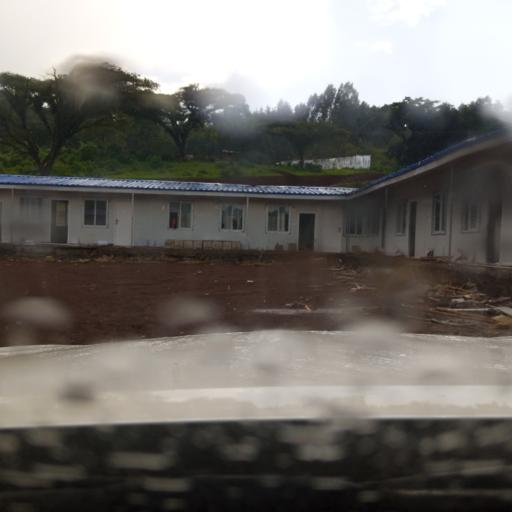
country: ET
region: Oromiya
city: Agaro
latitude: 7.9405
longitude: 36.8405
